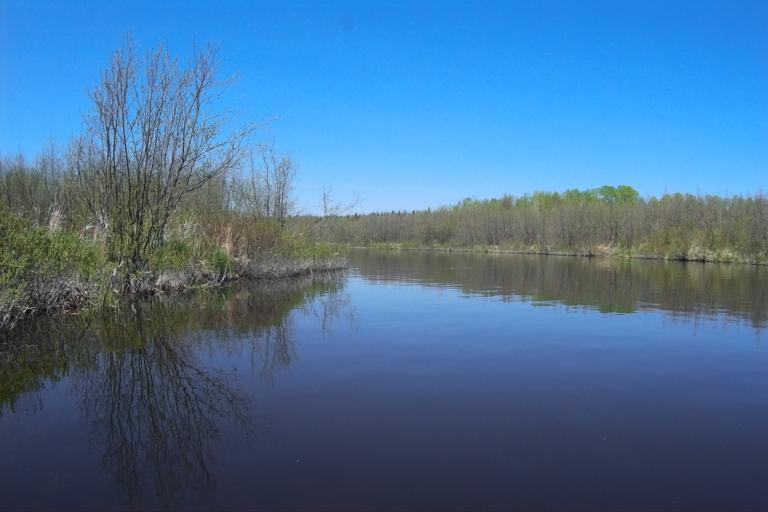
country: CA
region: Ontario
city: Powassan
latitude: 46.1577
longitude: -79.2488
